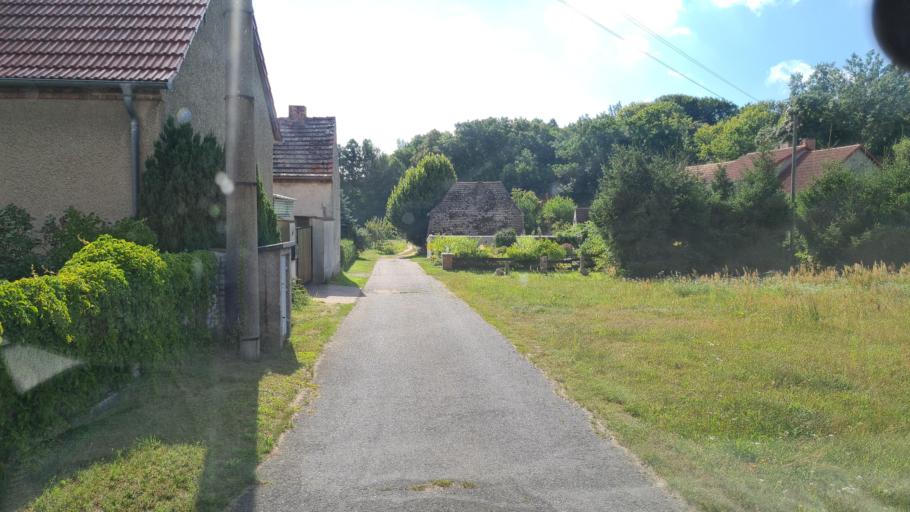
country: DE
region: Brandenburg
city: Crinitz
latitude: 51.7475
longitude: 13.7000
